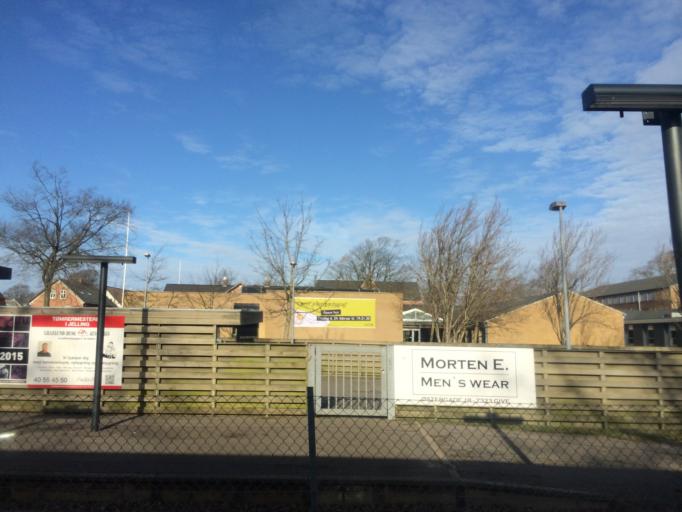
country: DK
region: South Denmark
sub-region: Vejle Kommune
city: Jelling
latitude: 55.7540
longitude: 9.4209
